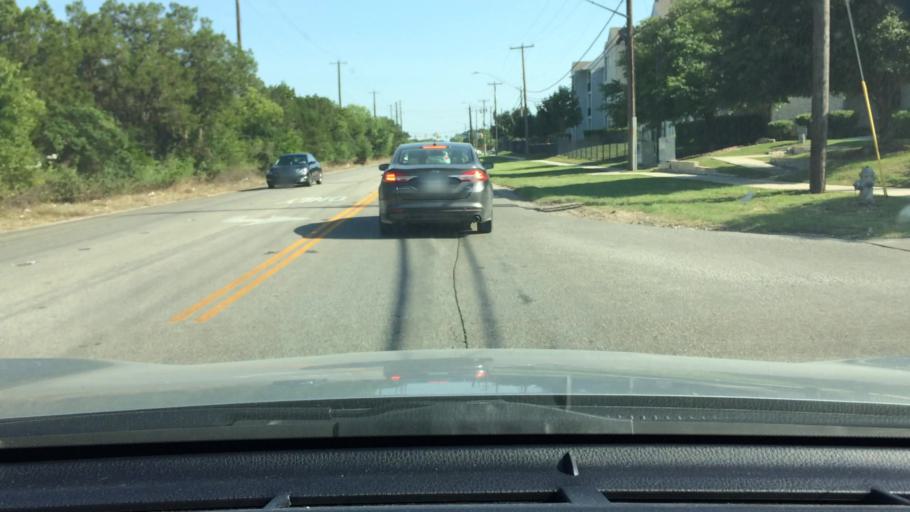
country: US
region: Texas
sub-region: Bexar County
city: Helotes
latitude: 29.5748
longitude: -98.6318
